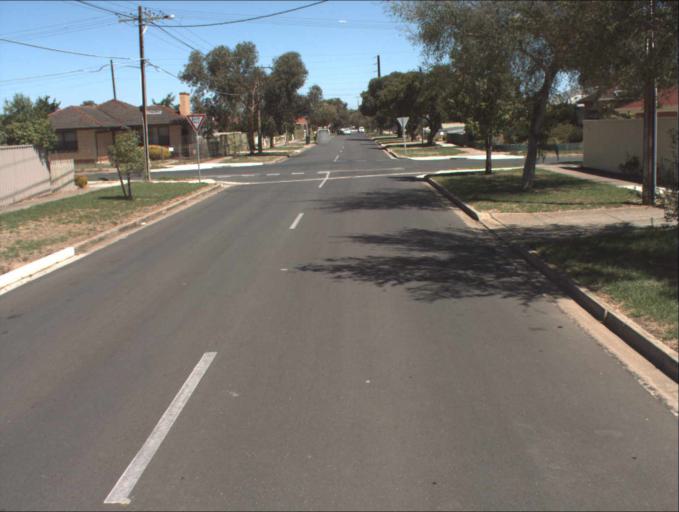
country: AU
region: South Australia
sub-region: Port Adelaide Enfield
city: Enfield
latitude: -34.8567
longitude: 138.6168
